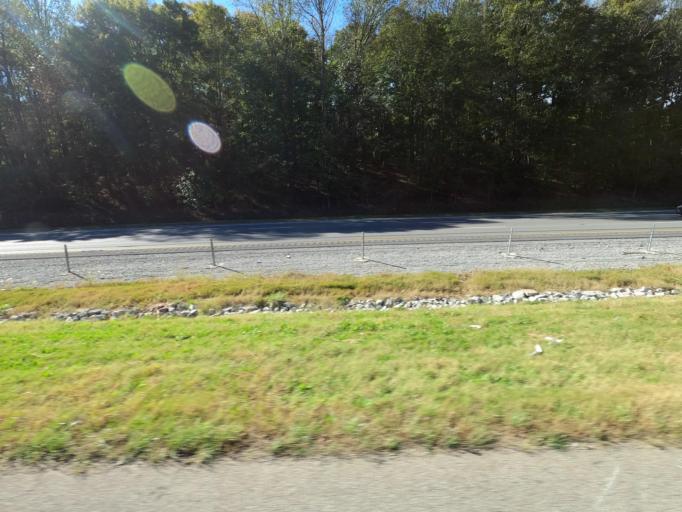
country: US
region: Tennessee
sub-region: Dickson County
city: White Bluff
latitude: 36.0264
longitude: -87.1971
